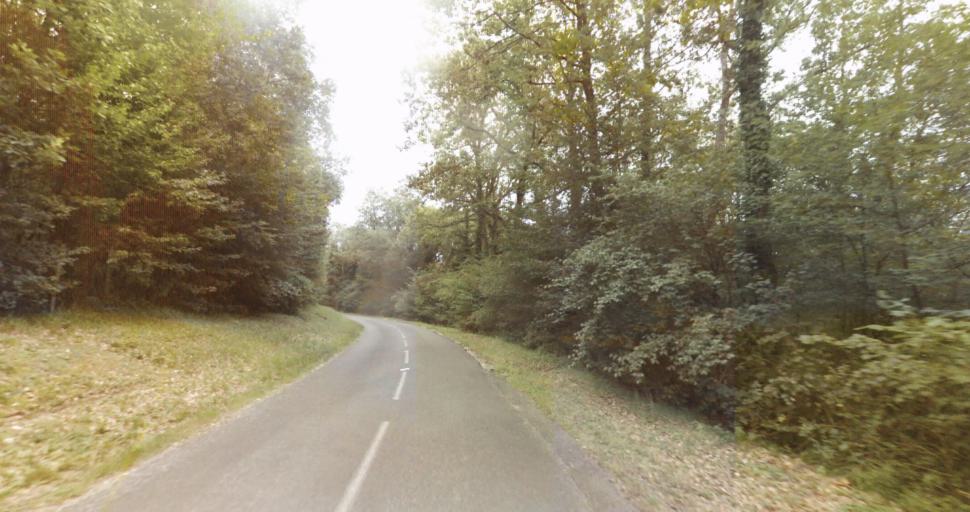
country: FR
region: Haute-Normandie
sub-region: Departement de l'Eure
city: Croth
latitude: 48.8527
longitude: 1.3646
